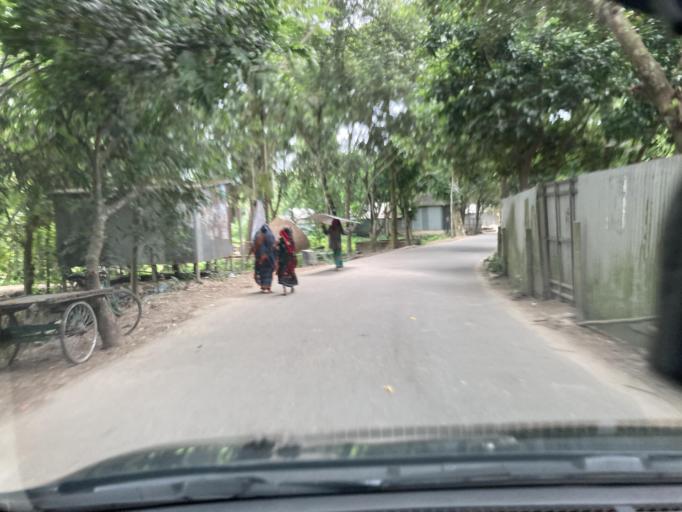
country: BD
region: Dhaka
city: Dohar
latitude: 23.7940
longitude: 90.0531
